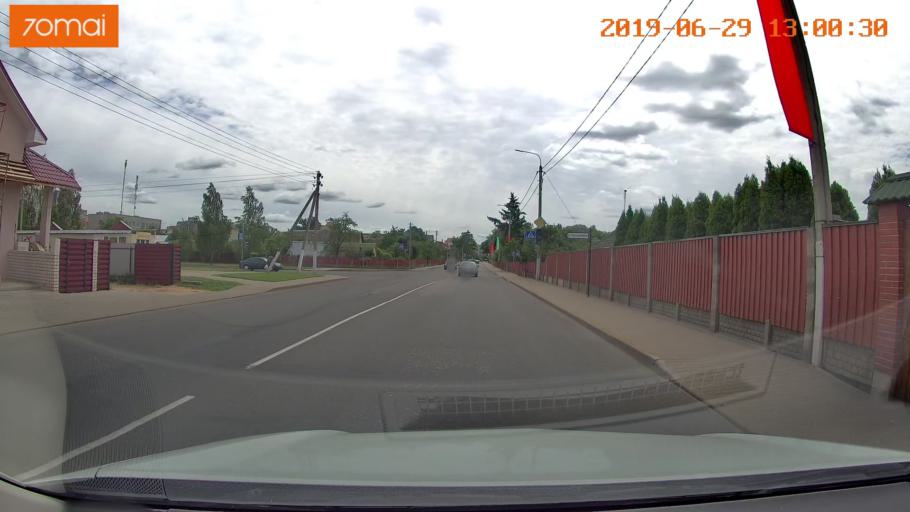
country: BY
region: Minsk
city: Slutsk
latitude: 53.0442
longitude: 27.5572
